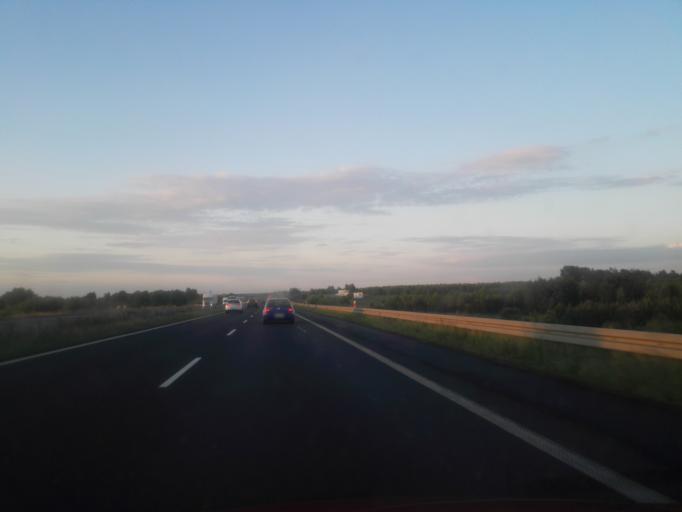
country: PL
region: Silesian Voivodeship
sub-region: Powiat czestochowski
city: Koscielec
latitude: 50.8933
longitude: 19.1851
